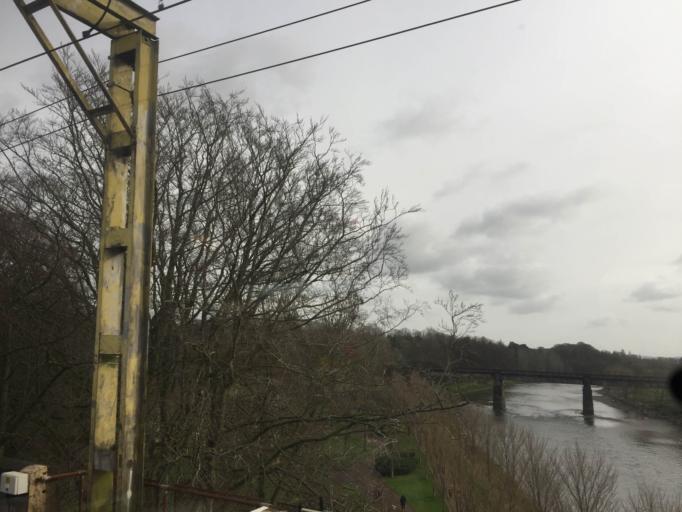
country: GB
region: England
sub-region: Lancashire
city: Preston
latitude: 53.7504
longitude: -2.7062
